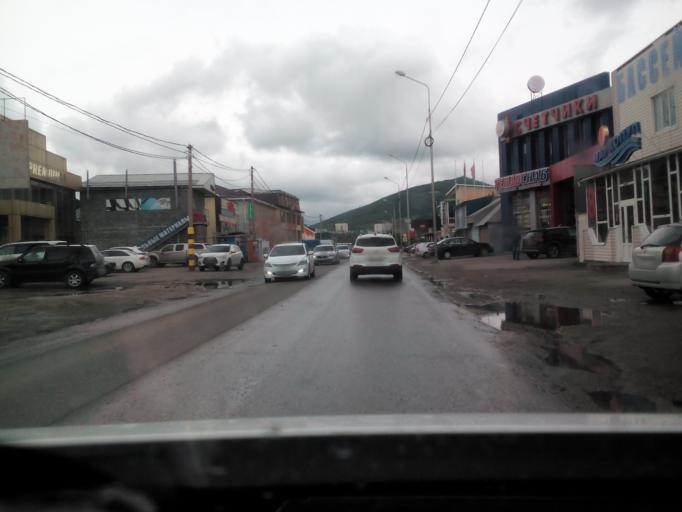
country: RU
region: Stavropol'skiy
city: Pyatigorsk
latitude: 44.0594
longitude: 43.0349
